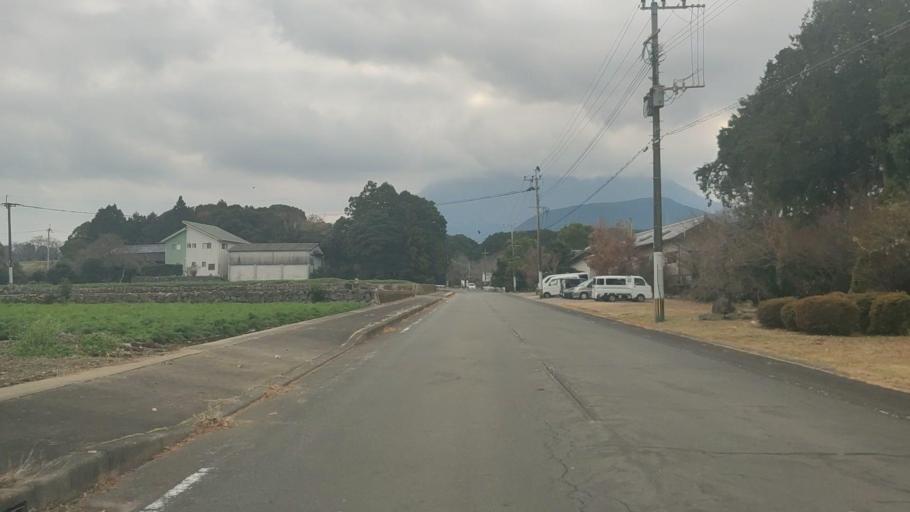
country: JP
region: Nagasaki
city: Shimabara
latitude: 32.8208
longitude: 130.2911
